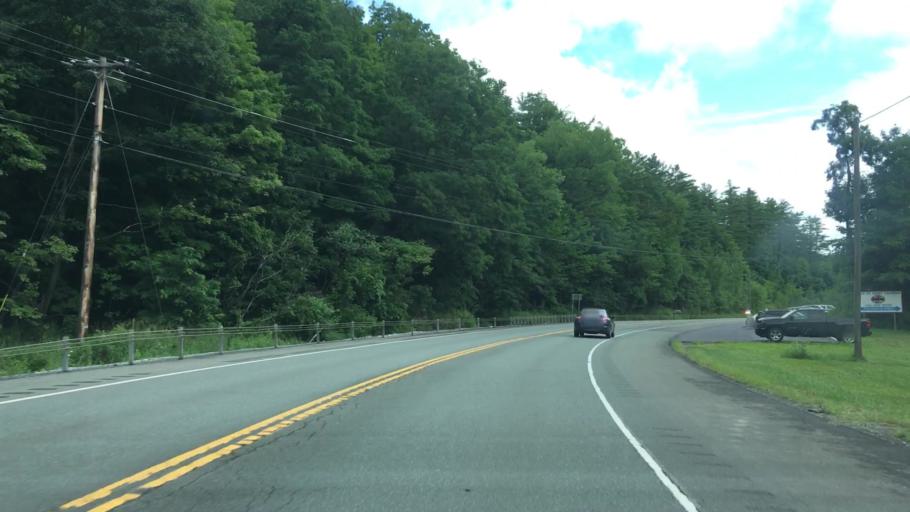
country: US
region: New York
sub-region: Rensselaer County
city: Hoosick Falls
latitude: 42.8464
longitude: -73.3644
